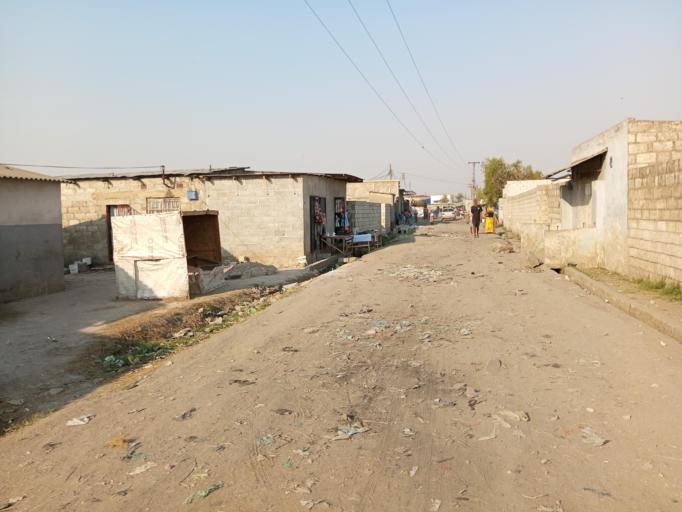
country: ZM
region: Lusaka
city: Lusaka
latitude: -15.3899
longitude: 28.2898
